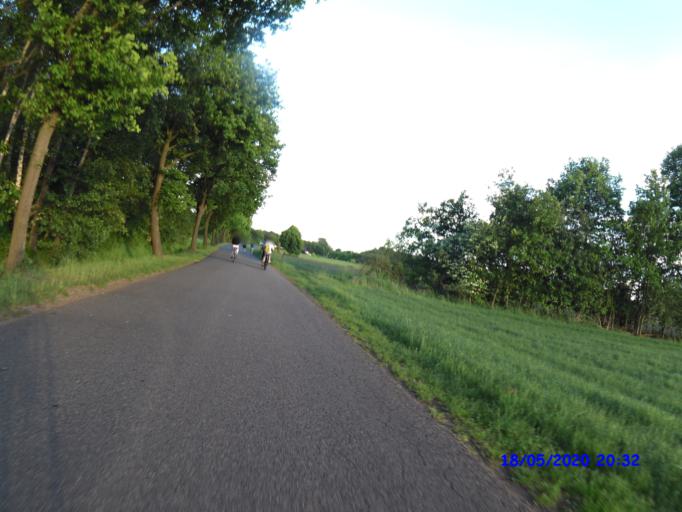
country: BE
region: Flanders
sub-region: Provincie Antwerpen
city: Kasterlee
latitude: 51.1976
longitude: 4.9523
